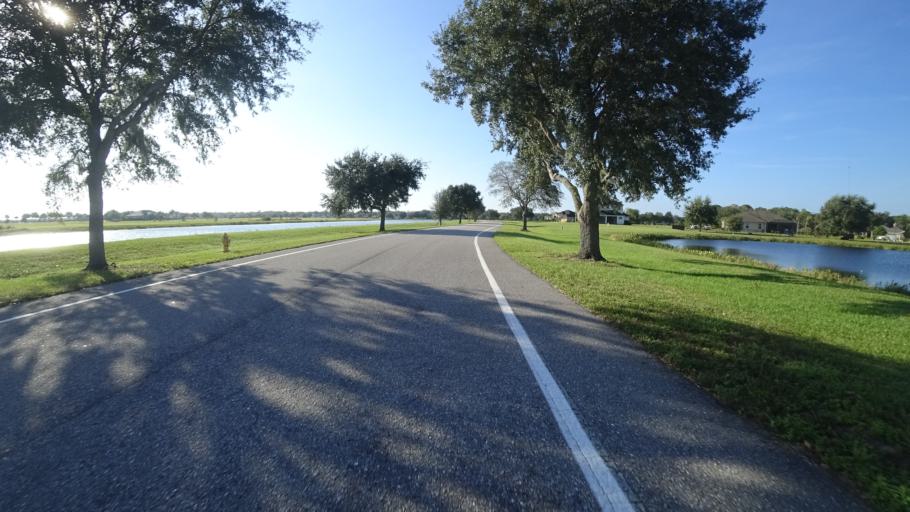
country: US
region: Florida
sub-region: Hillsborough County
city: Sun City Center
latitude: 27.5663
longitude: -82.3564
